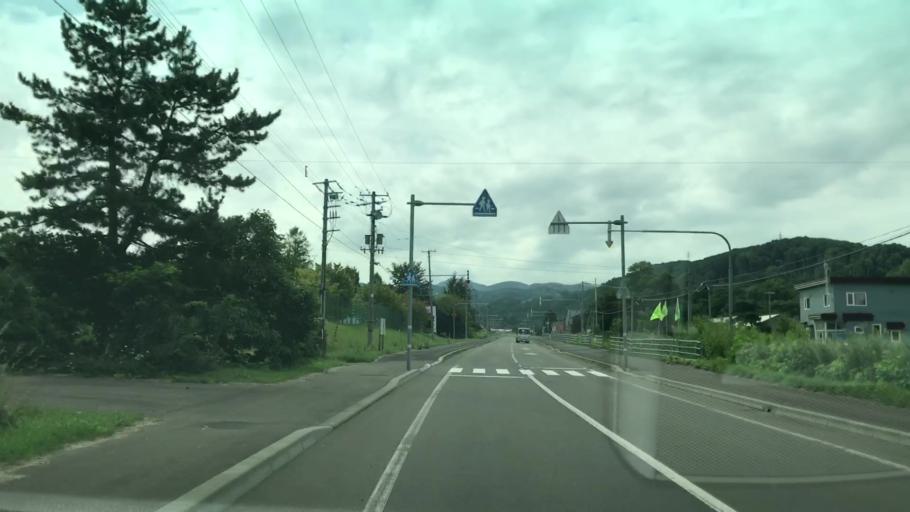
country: JP
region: Hokkaido
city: Yoichi
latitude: 43.1822
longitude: 140.8449
